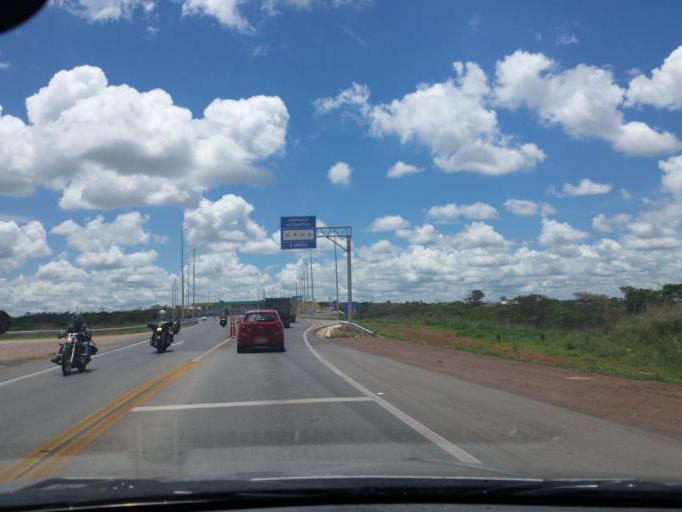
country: BR
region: Goias
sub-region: Cristalina
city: Cristalina
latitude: -16.7358
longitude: -47.6200
